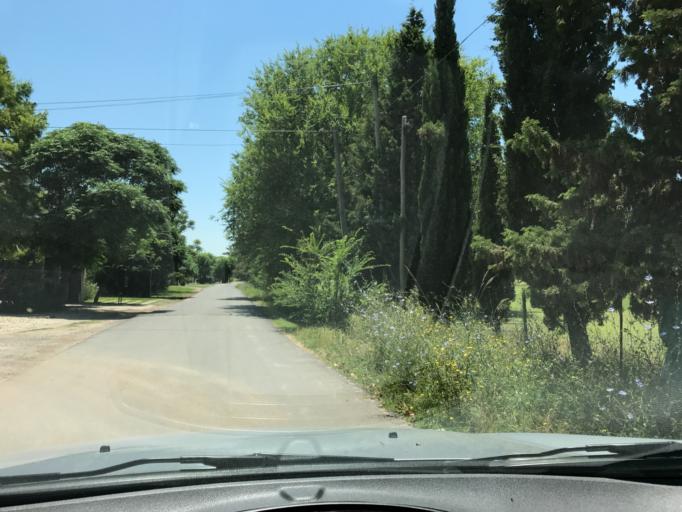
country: AR
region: Buenos Aires
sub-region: Partido de La Plata
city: La Plata
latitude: -34.8612
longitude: -58.0479
